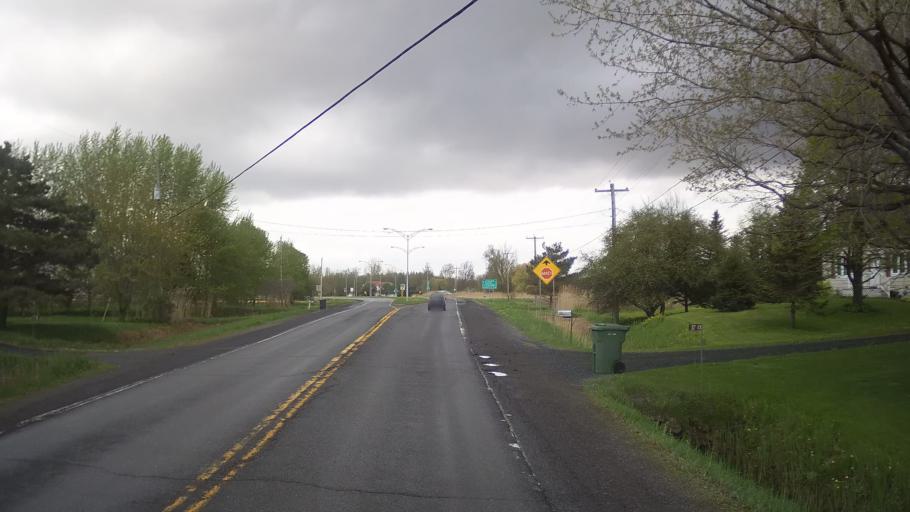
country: CA
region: Quebec
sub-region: Monteregie
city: Rougemont
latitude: 45.3485
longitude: -73.1023
